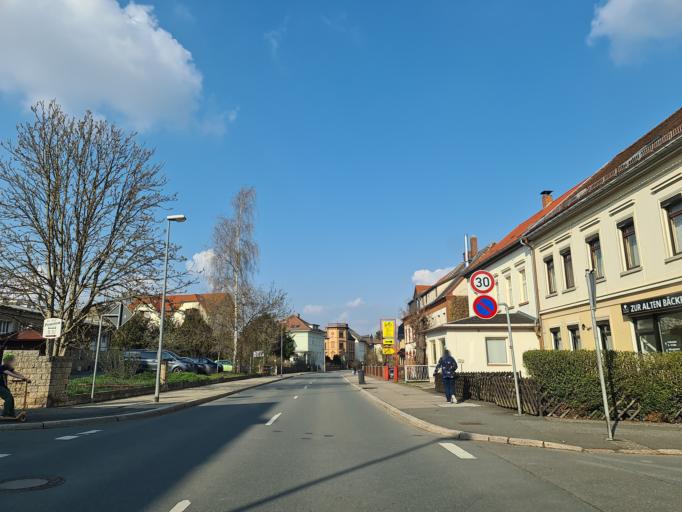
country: DE
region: Thuringia
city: Eisenberg
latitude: 50.9653
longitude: 11.8927
